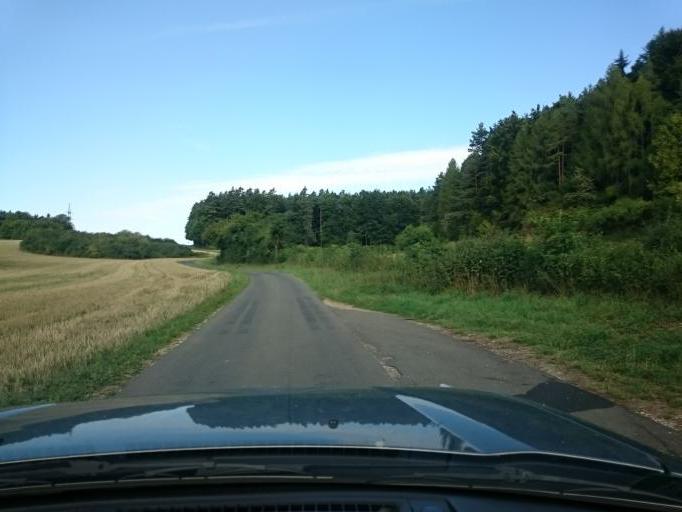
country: DE
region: Bavaria
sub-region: Upper Palatinate
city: Hirschbach
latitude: 49.5543
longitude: 11.5174
